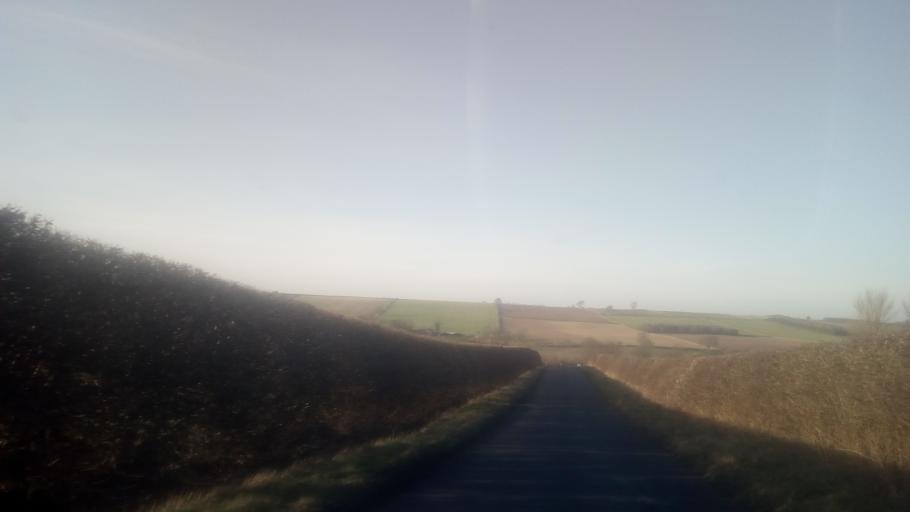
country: GB
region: Scotland
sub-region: The Scottish Borders
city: Jedburgh
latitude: 55.4931
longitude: -2.6013
